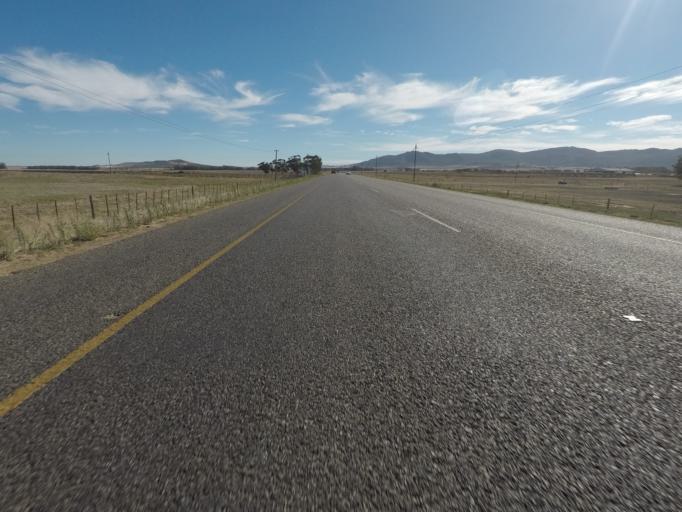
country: ZA
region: Western Cape
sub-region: West Coast District Municipality
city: Malmesbury
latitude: -33.6347
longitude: 18.7200
